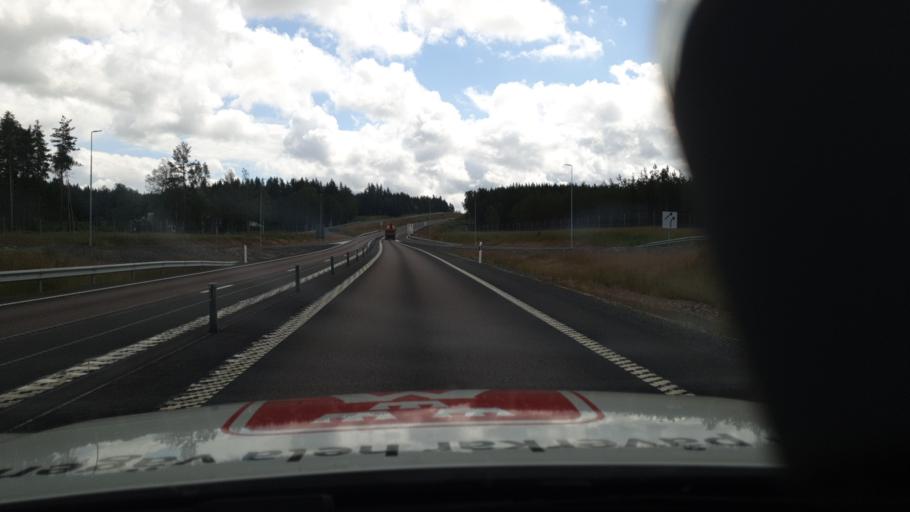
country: SE
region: Joenkoeping
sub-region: Mullsjo Kommun
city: Mullsjoe
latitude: 57.8872
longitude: 13.8967
